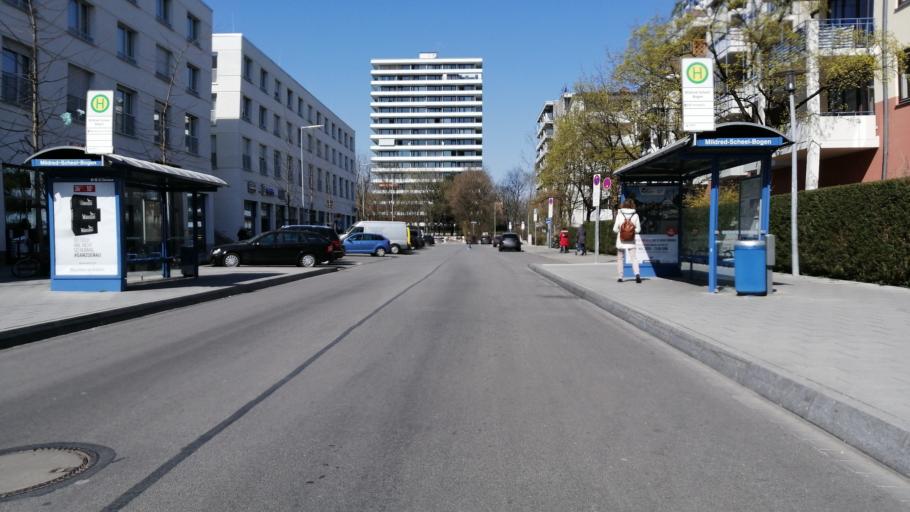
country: DE
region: Bavaria
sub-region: Upper Bavaria
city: Munich
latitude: 48.1752
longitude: 11.5819
